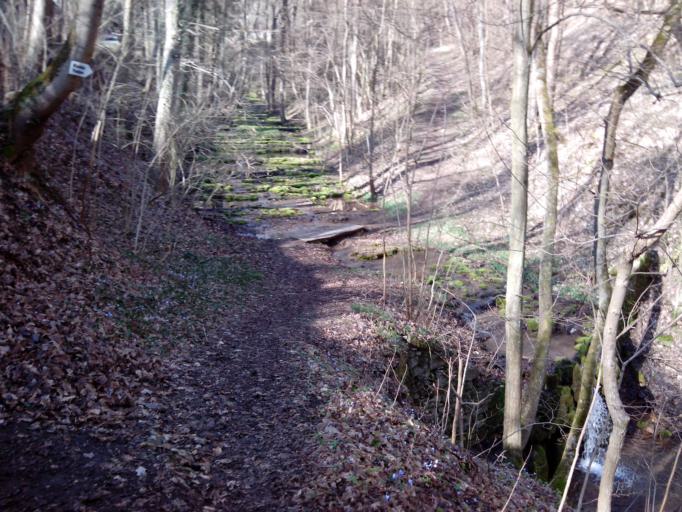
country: CZ
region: Central Bohemia
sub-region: Okres Beroun
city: Beroun
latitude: 49.9327
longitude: 14.1190
